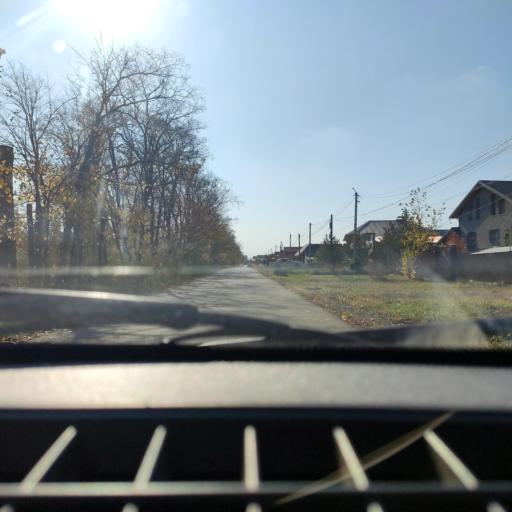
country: RU
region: Bashkortostan
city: Ufa
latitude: 54.6272
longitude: 55.9153
